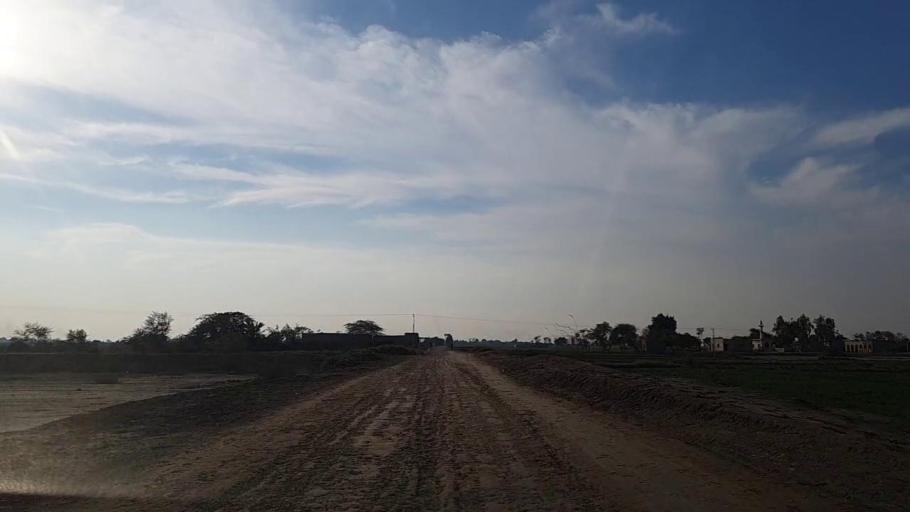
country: PK
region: Sindh
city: Bandhi
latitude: 26.5534
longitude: 68.2508
